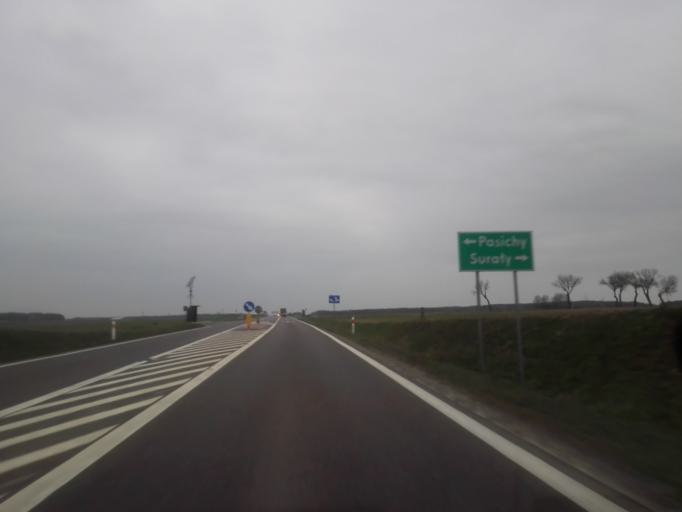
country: PL
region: Podlasie
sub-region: Powiat grajewski
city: Szczuczyn
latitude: 53.5011
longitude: 22.2330
